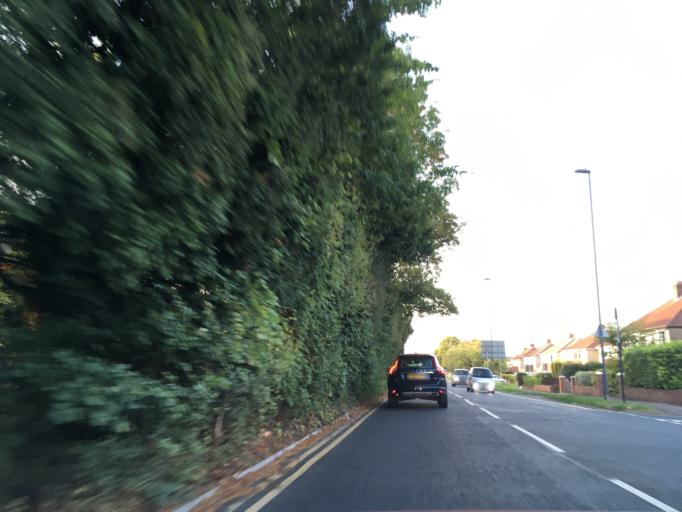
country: GB
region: England
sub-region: South Gloucestershire
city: Mangotsfield
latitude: 51.4936
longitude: -2.5097
